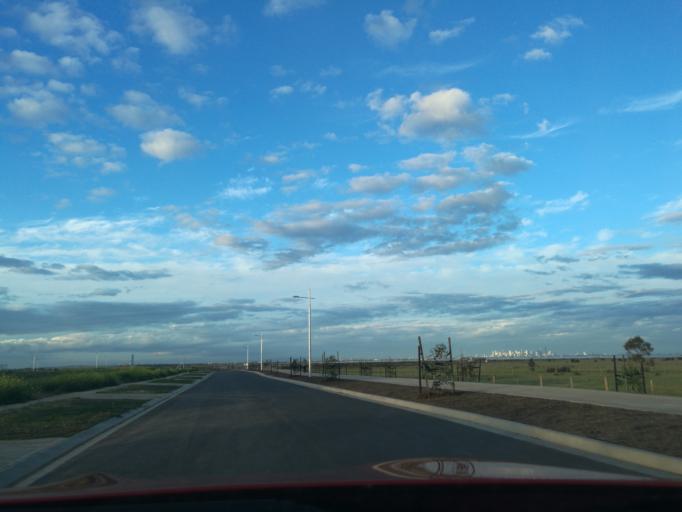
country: AU
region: Victoria
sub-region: Hobsons Bay
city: Altona Meadows
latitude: -37.9154
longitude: 144.7890
